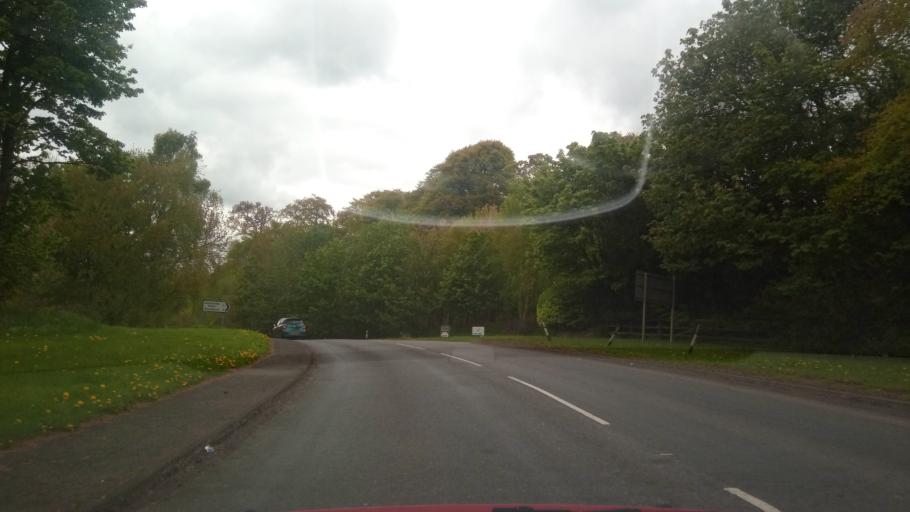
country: GB
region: Scotland
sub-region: The Scottish Borders
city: Melrose
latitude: 55.6092
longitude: -2.7528
